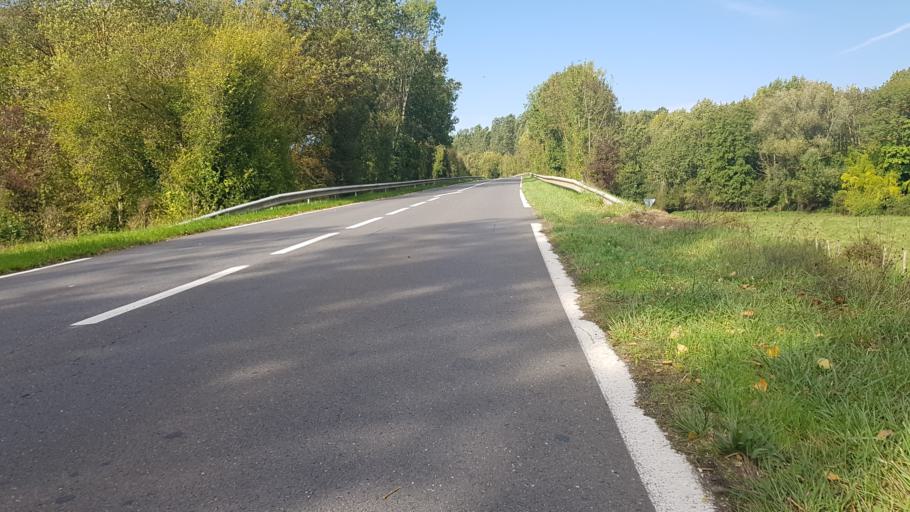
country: FR
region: Poitou-Charentes
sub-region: Departement de la Vienne
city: Chasseneuil-du-Poitou
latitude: 46.6335
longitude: 0.3630
